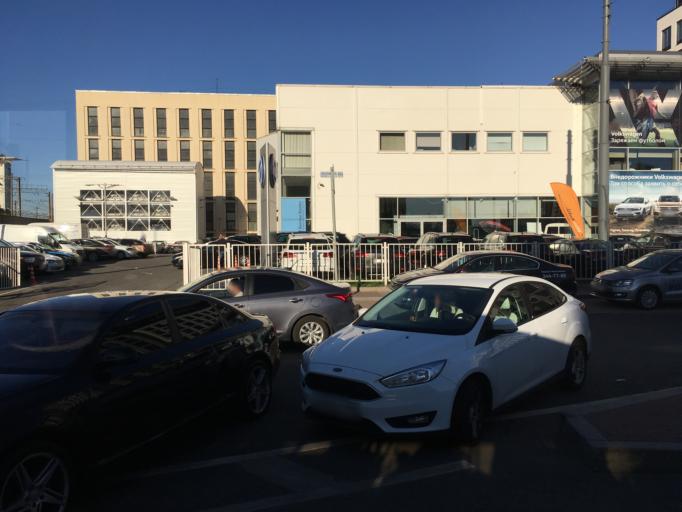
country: RU
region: St.-Petersburg
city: Admiralteisky
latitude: 59.8825
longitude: 30.3204
